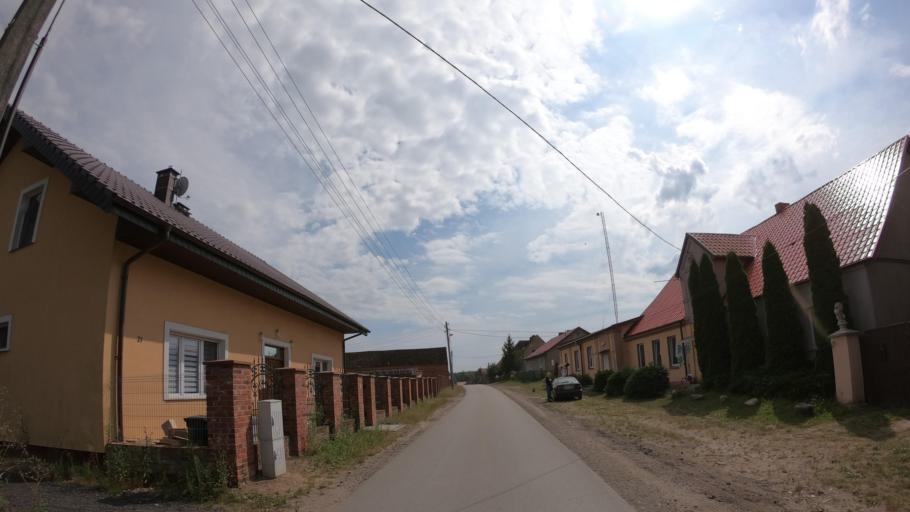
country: PL
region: West Pomeranian Voivodeship
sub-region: Powiat walecki
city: Tuczno
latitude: 53.2369
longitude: 16.1099
